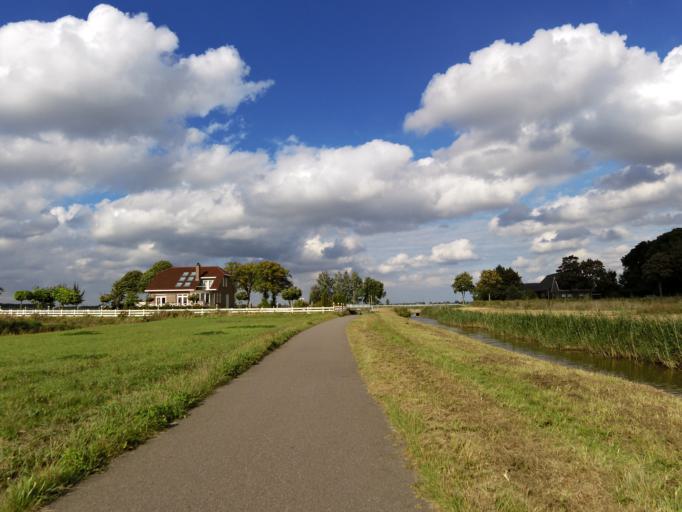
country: NL
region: South Holland
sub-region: Gemeente Waddinxveen
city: Groenswaard
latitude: 52.0759
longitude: 4.6068
